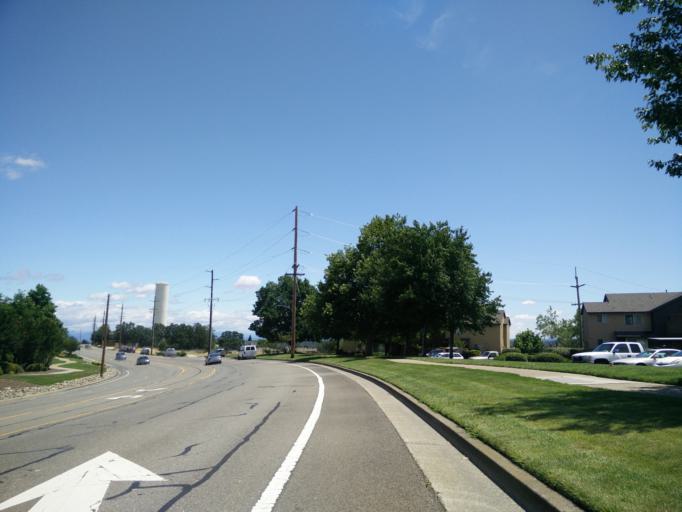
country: US
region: California
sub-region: Shasta County
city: Redding
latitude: 40.5980
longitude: -122.3705
